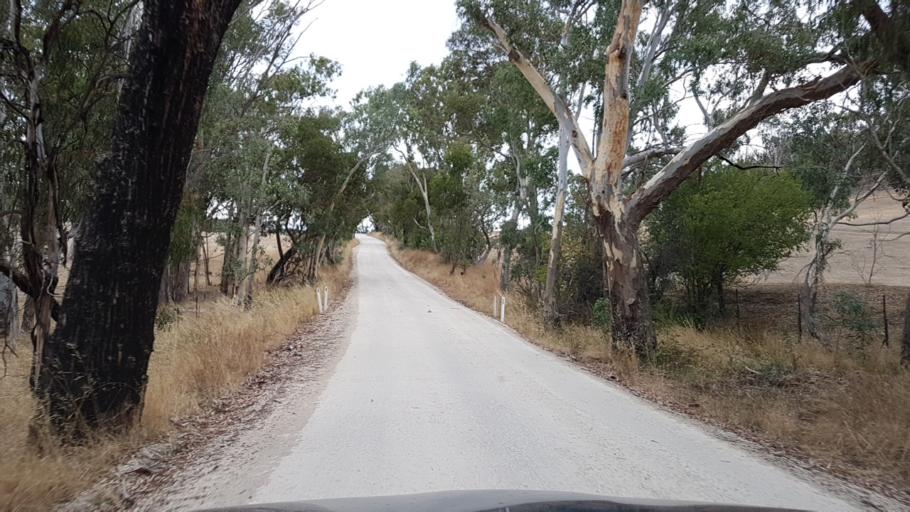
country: AU
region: South Australia
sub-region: Adelaide Hills
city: Gumeracha
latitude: -34.7962
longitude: 138.8339
